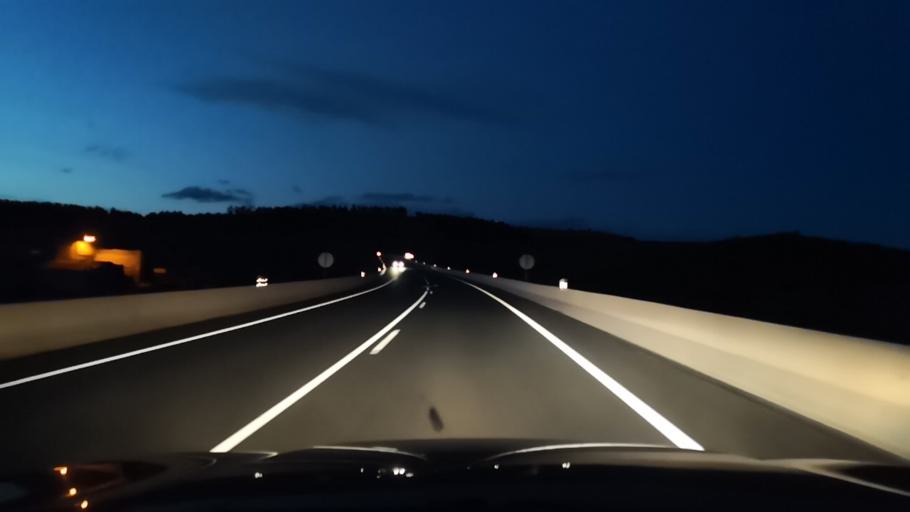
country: PT
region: Braganca
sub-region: Mogadouro
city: Mogadouro
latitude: 41.2784
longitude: -6.7408
